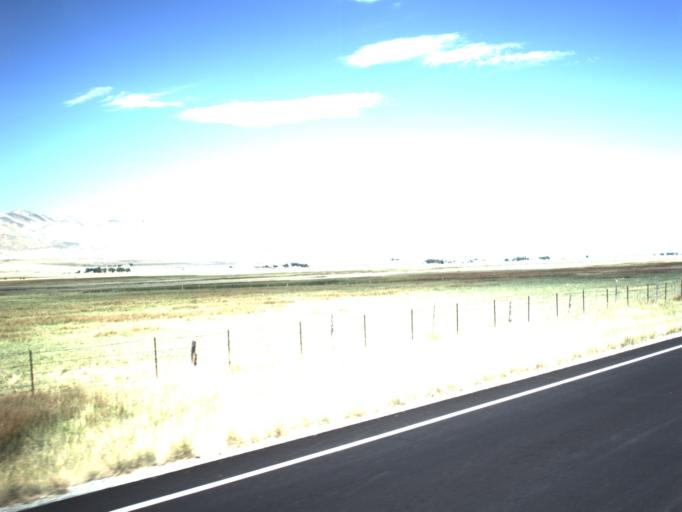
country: US
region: Utah
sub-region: Box Elder County
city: Tremonton
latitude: 41.7435
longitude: -112.4343
